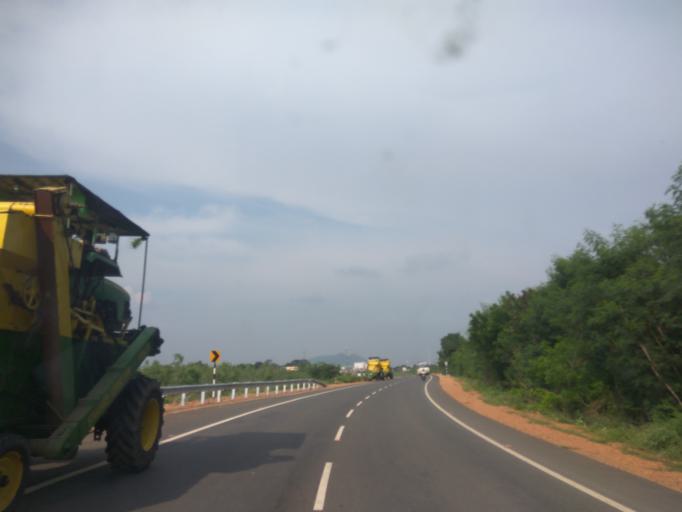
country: IN
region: Andhra Pradesh
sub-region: Prakasam
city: Chemmumiahpet
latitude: 15.8969
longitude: 79.2946
